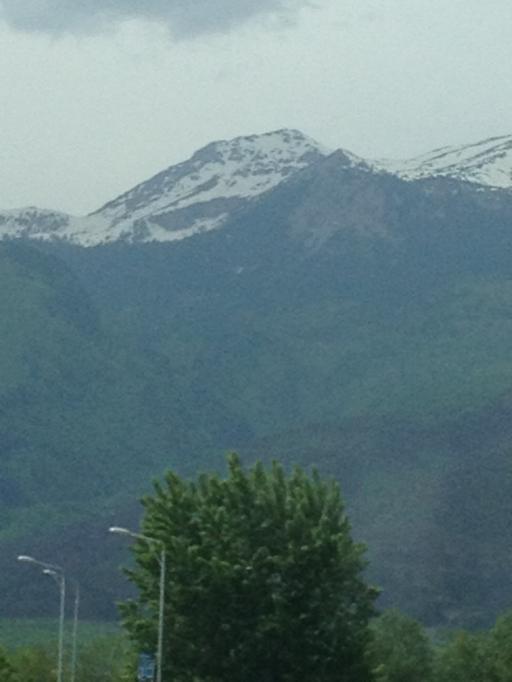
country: XK
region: Pec
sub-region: Komuna e Pejes
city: Peje
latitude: 42.6458
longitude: 20.3148
